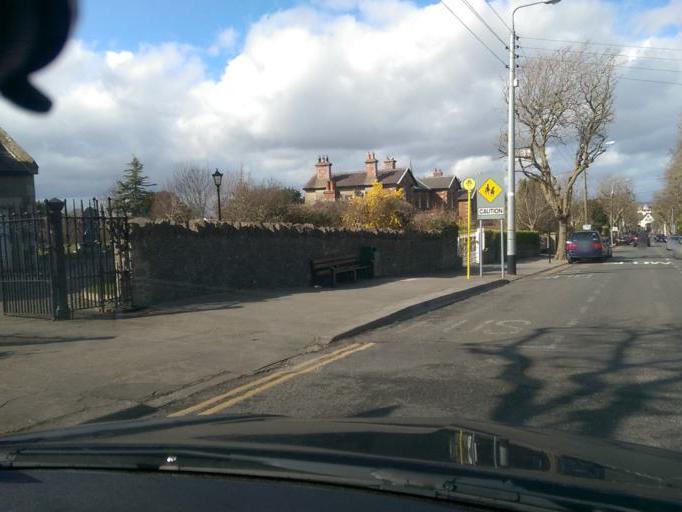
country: IE
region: Leinster
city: Malahide
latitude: 53.4482
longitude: -6.1531
